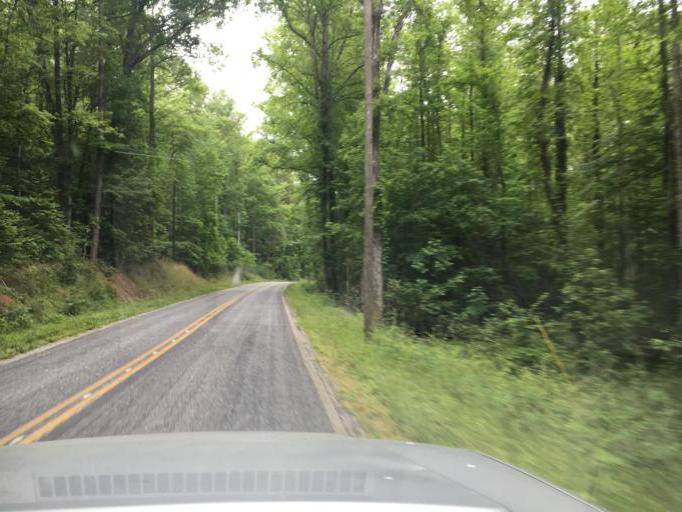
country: US
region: South Carolina
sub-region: Greenville County
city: Tigerville
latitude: 35.1345
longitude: -82.4066
